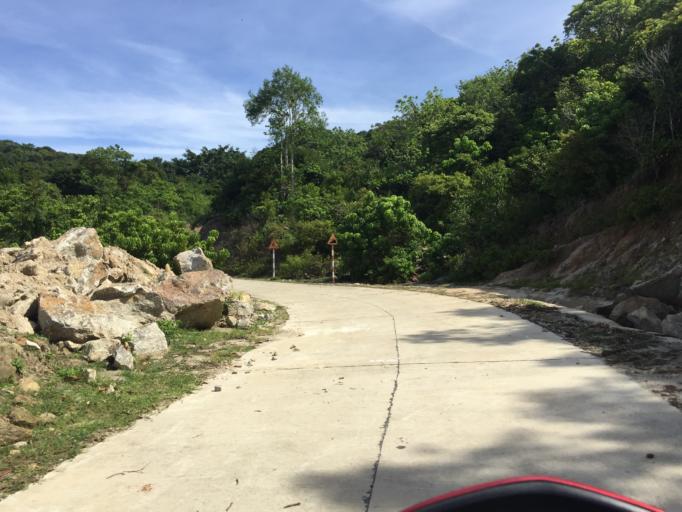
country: VN
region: Quang Nam
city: Hoi An
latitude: 15.9367
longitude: 108.5328
